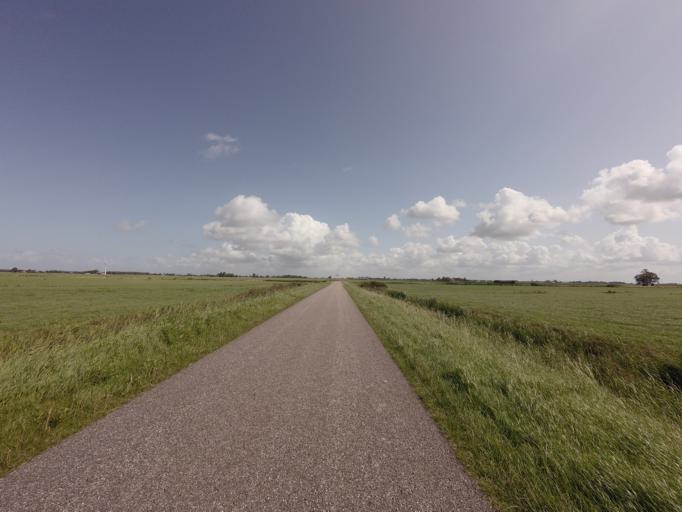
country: NL
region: Friesland
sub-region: Sudwest Fryslan
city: Makkum
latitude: 53.0668
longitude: 5.4552
